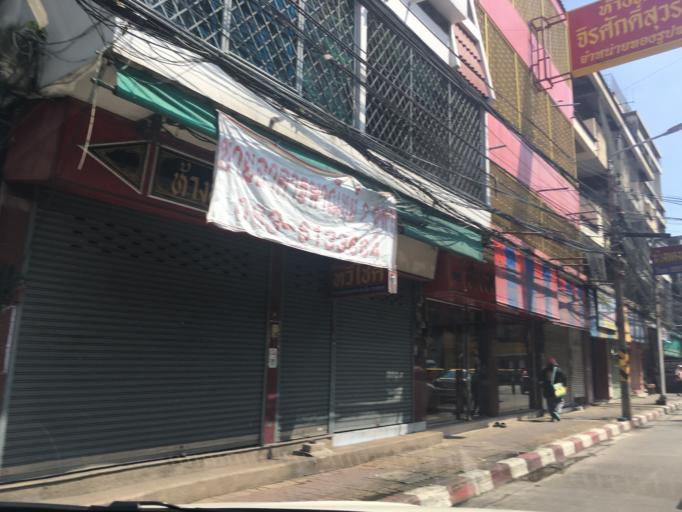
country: TH
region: Chon Buri
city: Chon Buri
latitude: 13.3635
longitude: 100.9856
